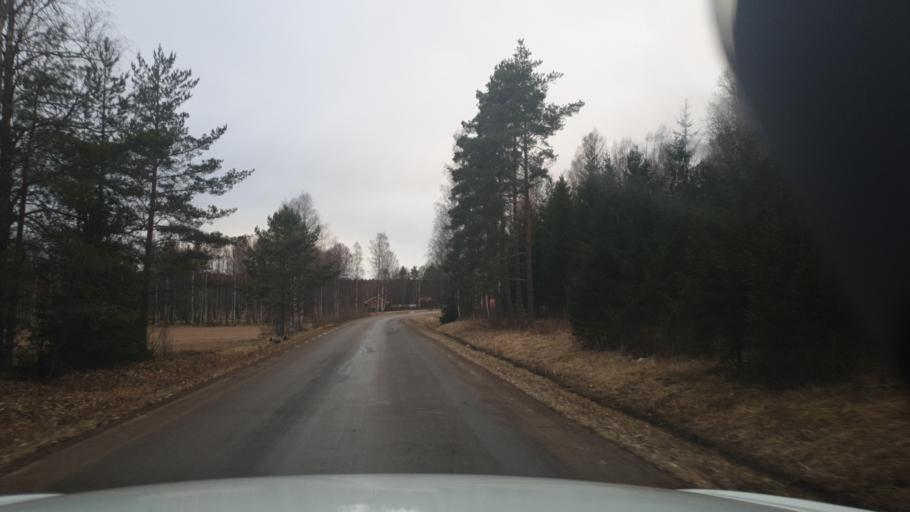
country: SE
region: Vaermland
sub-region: Arvika Kommun
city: Arvika
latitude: 59.5504
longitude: 12.7404
